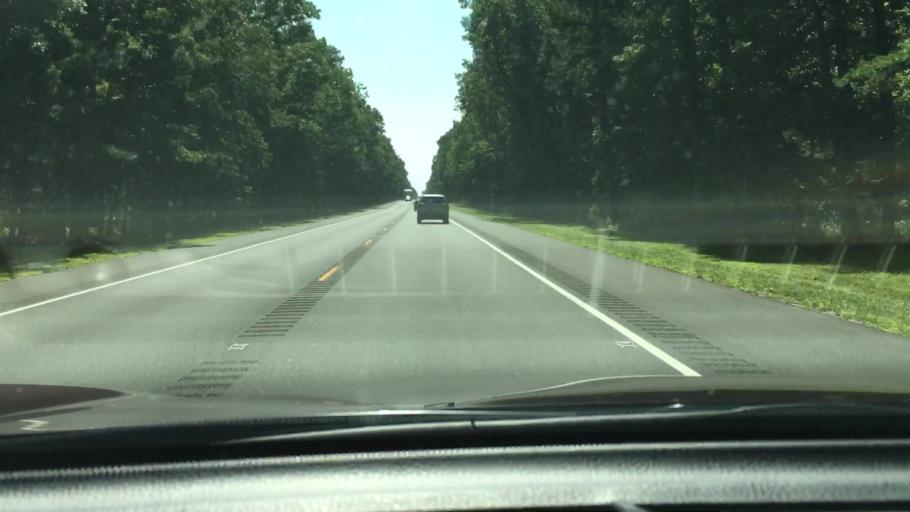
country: US
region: New Jersey
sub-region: Cumberland County
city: Laurel Lake
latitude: 39.3454
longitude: -74.9005
